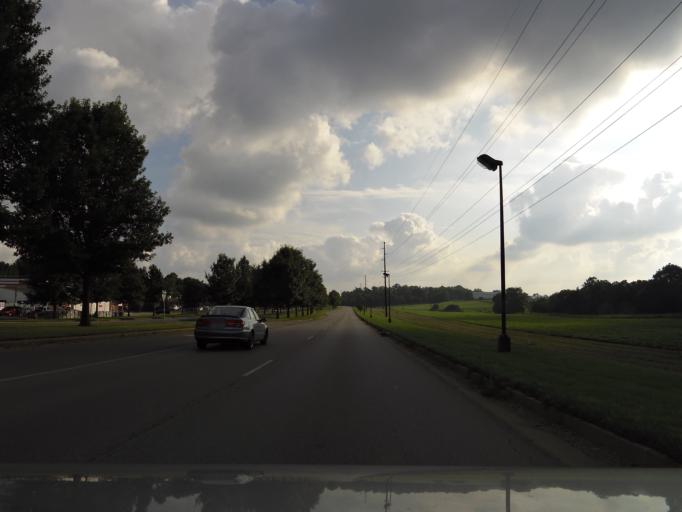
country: US
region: Kentucky
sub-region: Bourbon County
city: Paris
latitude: 38.1904
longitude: -84.2824
